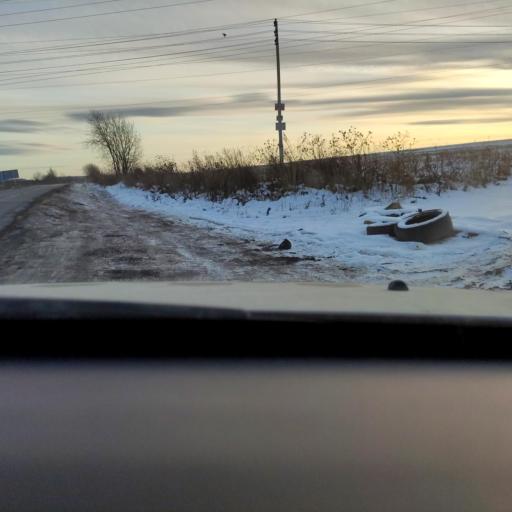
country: RU
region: Perm
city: Ferma
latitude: 57.9300
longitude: 56.3298
